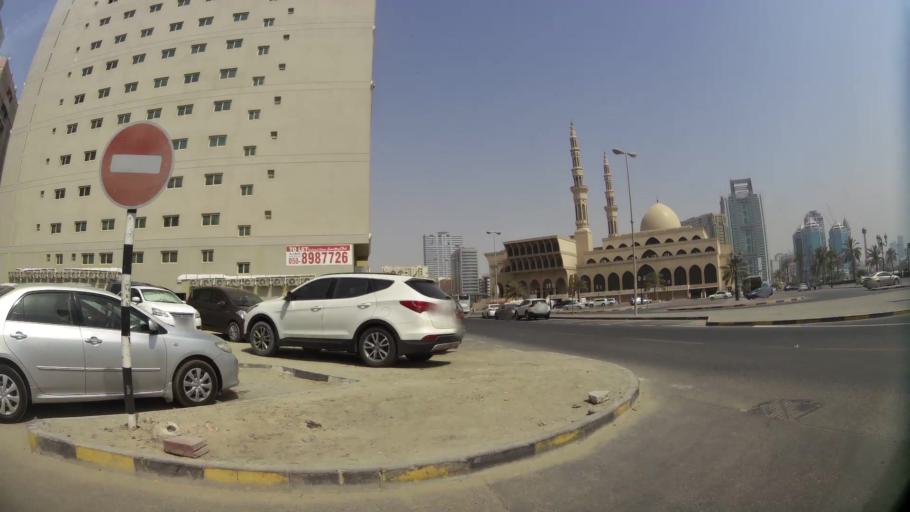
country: AE
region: Ash Shariqah
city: Sharjah
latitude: 25.3509
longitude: 55.3868
